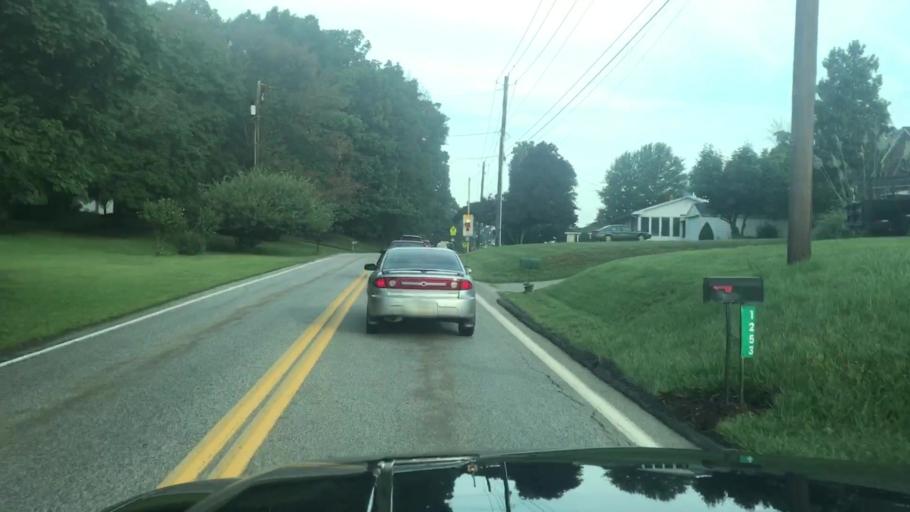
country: US
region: Pennsylvania
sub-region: Cumberland County
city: Shiremanstown
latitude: 40.2007
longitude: -76.9506
